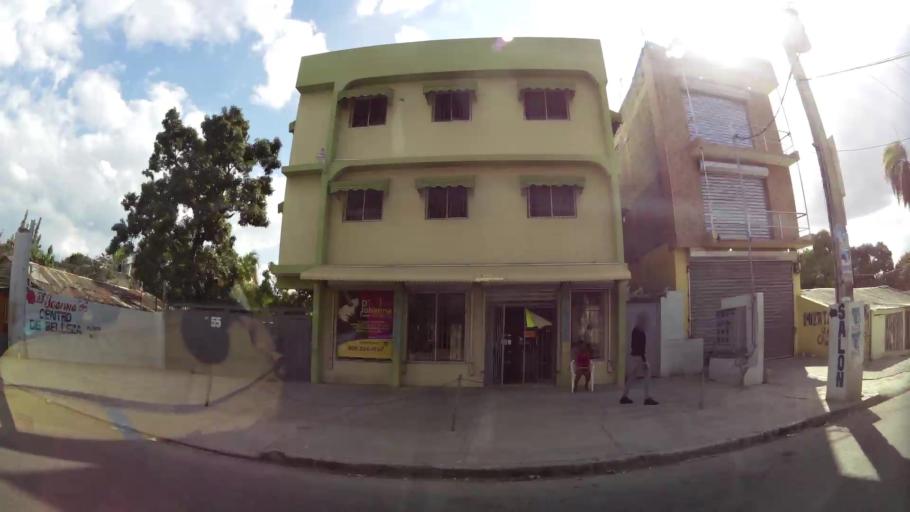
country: DO
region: Nacional
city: Ensanche Luperon
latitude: 18.5437
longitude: -69.8974
